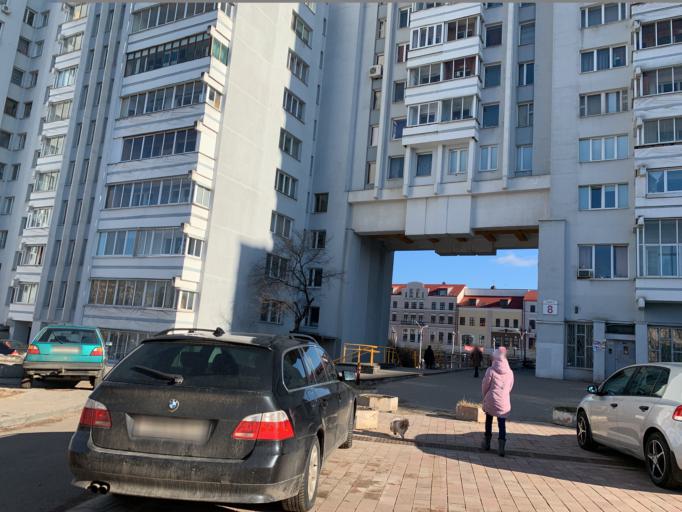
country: BY
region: Minsk
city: Minsk
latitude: 53.9045
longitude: 27.5502
